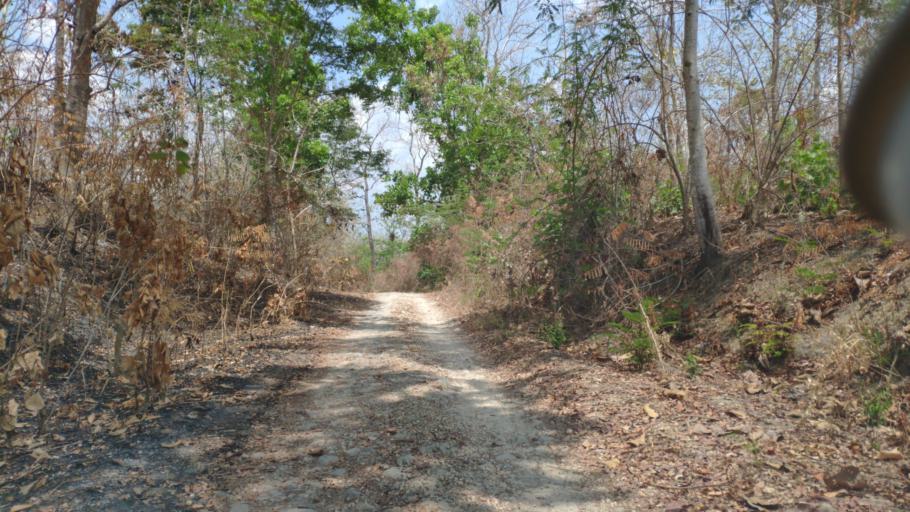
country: ID
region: Central Java
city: Suruhan
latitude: -6.9968
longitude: 111.5239
